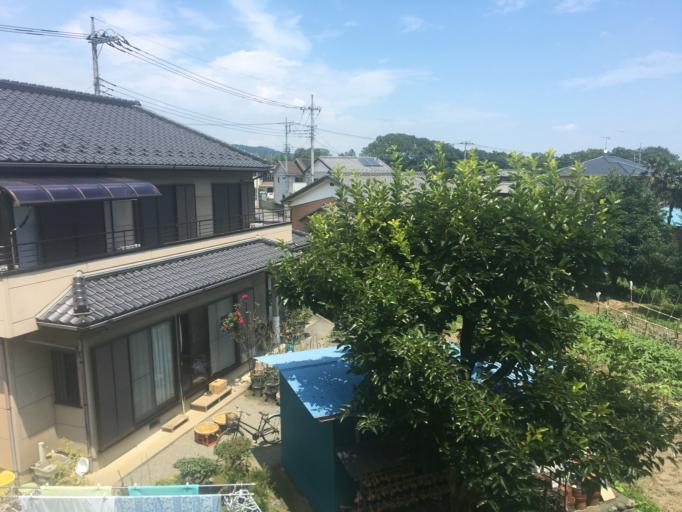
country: JP
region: Saitama
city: Yorii
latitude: 36.1090
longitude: 139.1854
